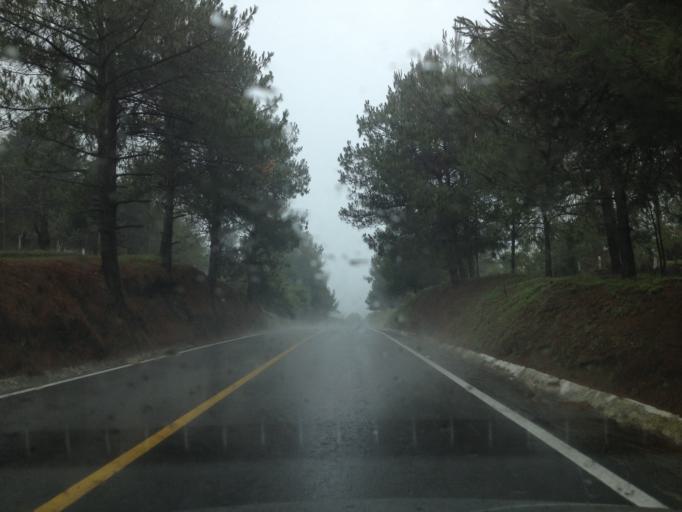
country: MX
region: Michoacan
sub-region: Patzcuaro
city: Santa Maria Huiramangaro (San Juan Tumbio)
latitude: 19.4891
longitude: -101.8024
